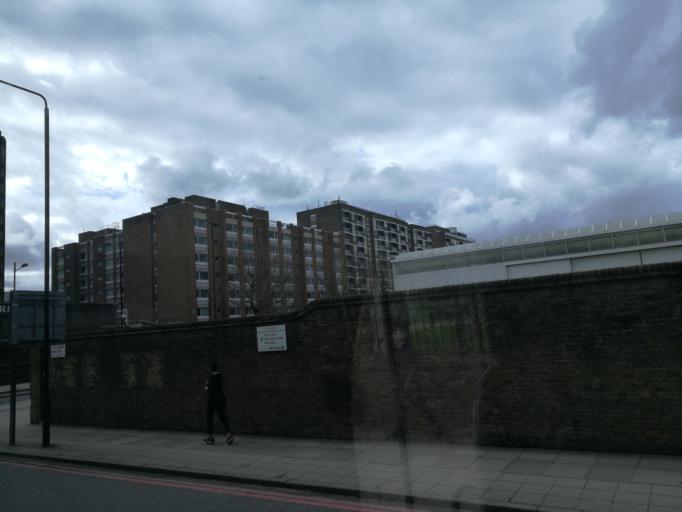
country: GB
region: England
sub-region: Greater London
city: Belsize Park
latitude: 51.5304
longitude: -0.1694
